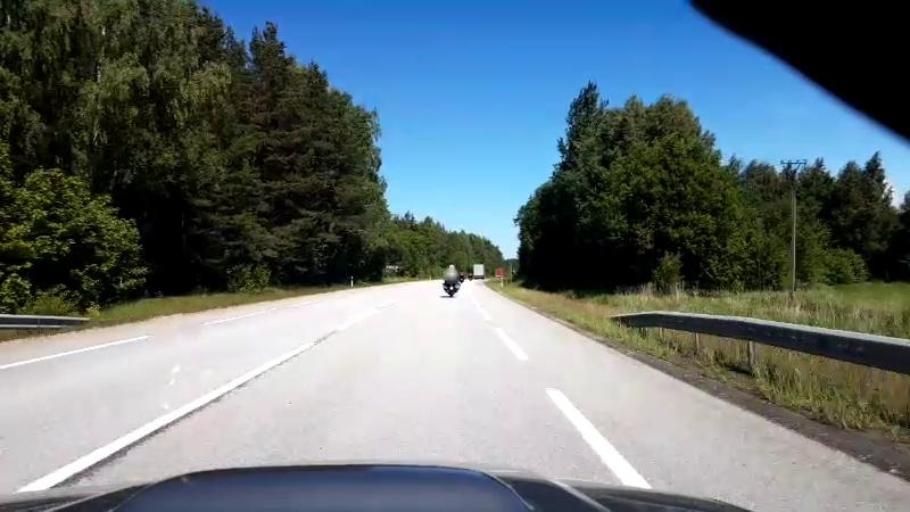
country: LV
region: Saulkrastu
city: Saulkrasti
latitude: 57.4200
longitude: 24.4288
